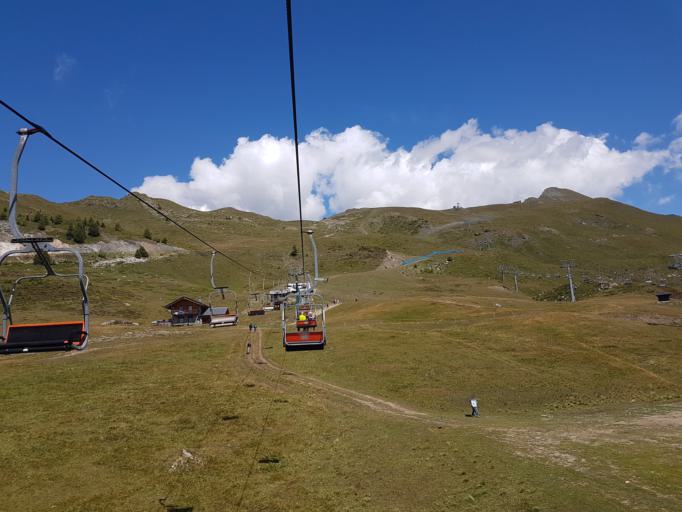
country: IT
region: Aosta Valley
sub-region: Valle d'Aosta
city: Chamois
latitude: 45.8488
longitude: 7.6324
